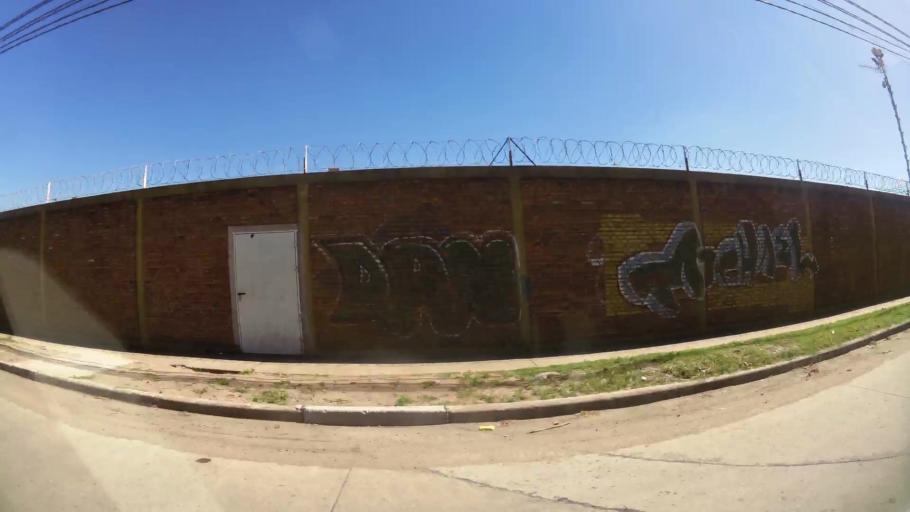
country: AR
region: Santa Fe
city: Perez
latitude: -32.9708
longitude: -60.7087
